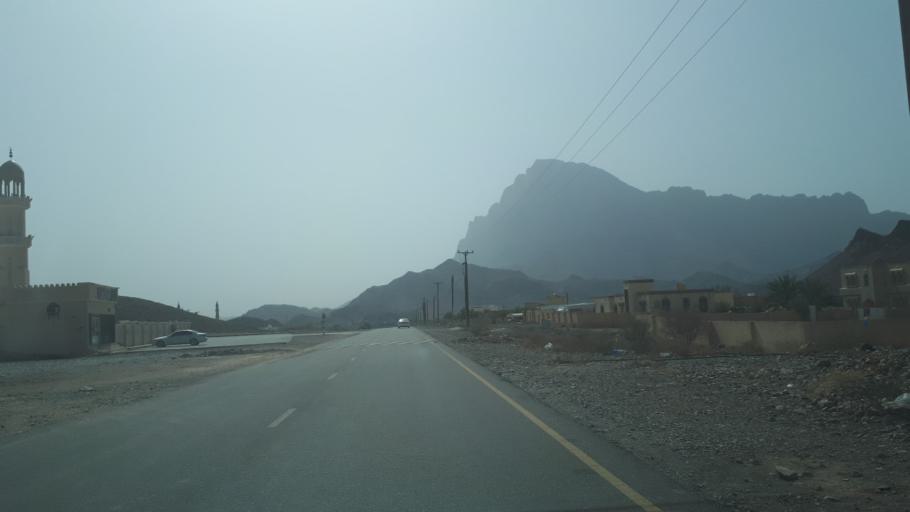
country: OM
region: Muhafazat ad Dakhiliyah
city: Bahla'
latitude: 23.2263
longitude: 57.0561
